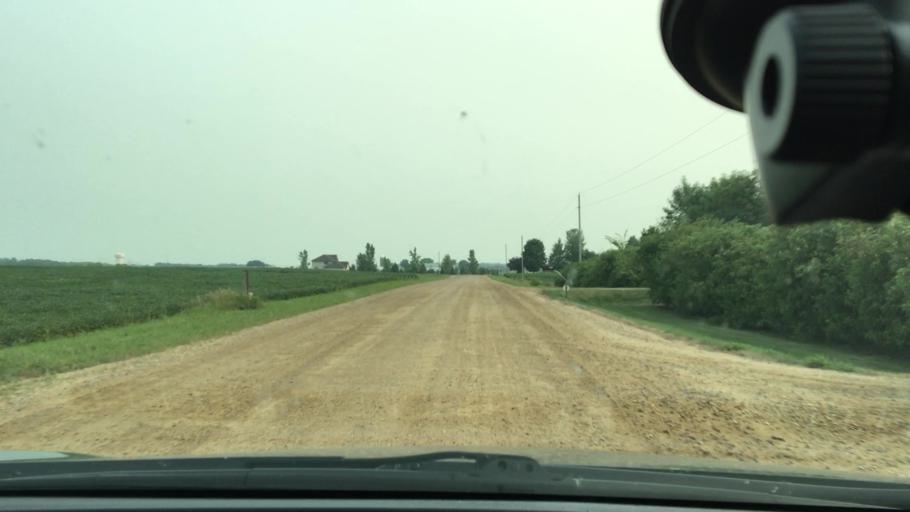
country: US
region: Minnesota
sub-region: Wright County
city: Albertville
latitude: 45.2474
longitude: -93.6273
